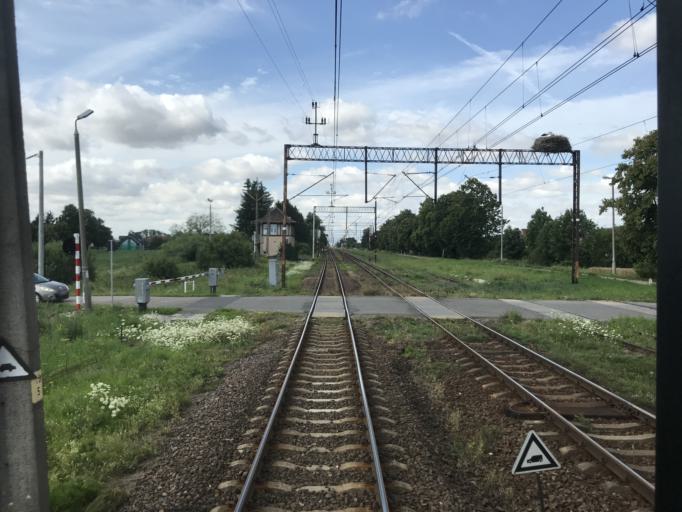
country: PL
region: Warmian-Masurian Voivodeship
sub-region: Powiat elblaski
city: Gronowo Elblaskie
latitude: 54.0918
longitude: 19.3108
